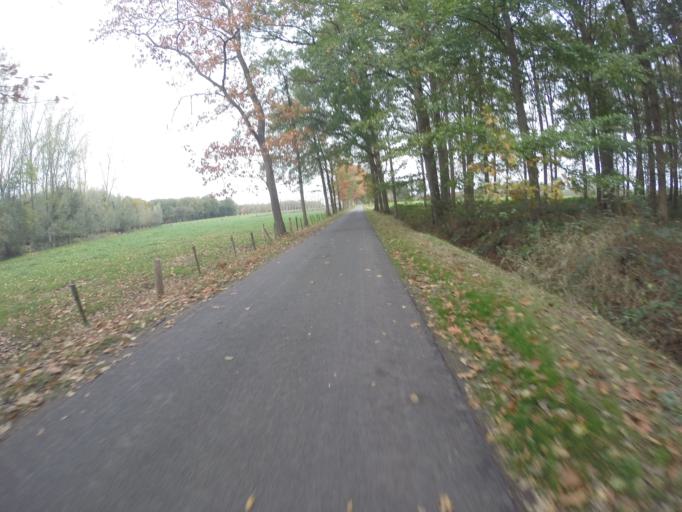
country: BE
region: Flanders
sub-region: Provincie Oost-Vlaanderen
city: Knesselare
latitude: 51.1710
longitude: 3.4256
